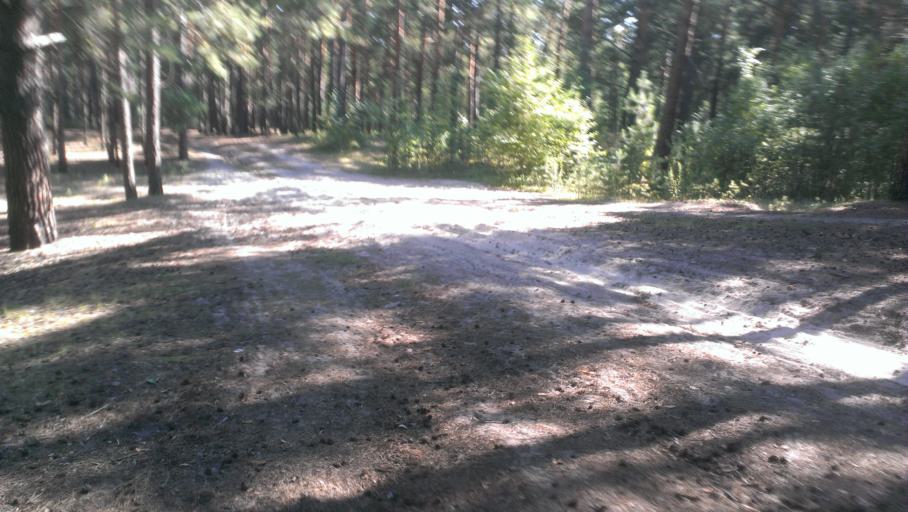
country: RU
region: Altai Krai
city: Yuzhnyy
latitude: 53.3170
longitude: 83.6877
